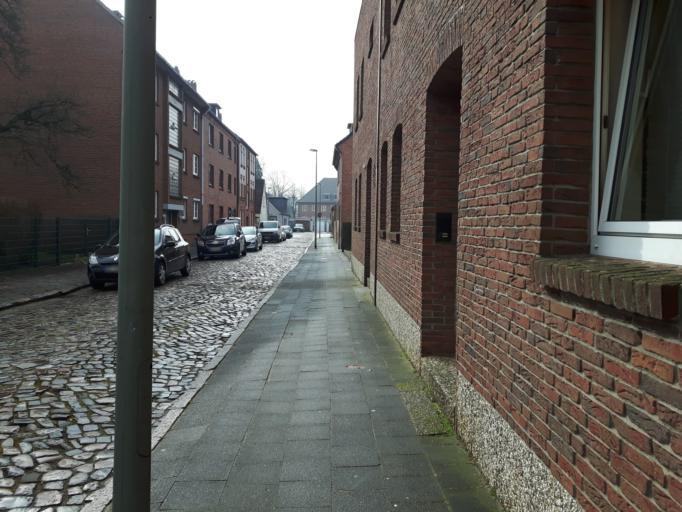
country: DE
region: Schleswig-Holstein
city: Neumunster
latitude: 54.0777
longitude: 9.9852
